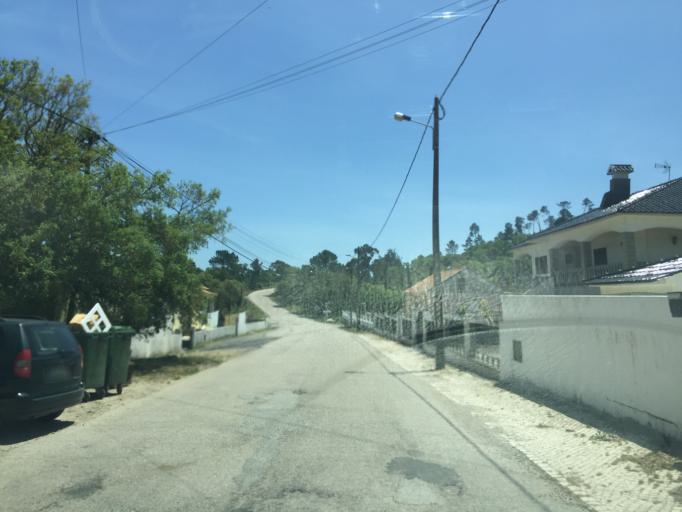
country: PT
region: Lisbon
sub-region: Mafra
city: Venda do Pinheiro
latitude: 38.8932
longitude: -9.2289
